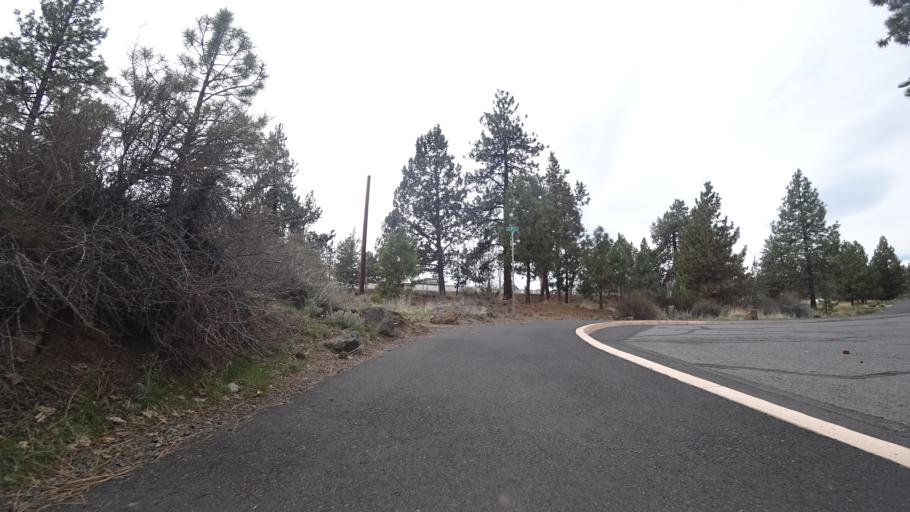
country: US
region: Oregon
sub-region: Deschutes County
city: Bend
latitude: 44.0538
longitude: -121.2927
